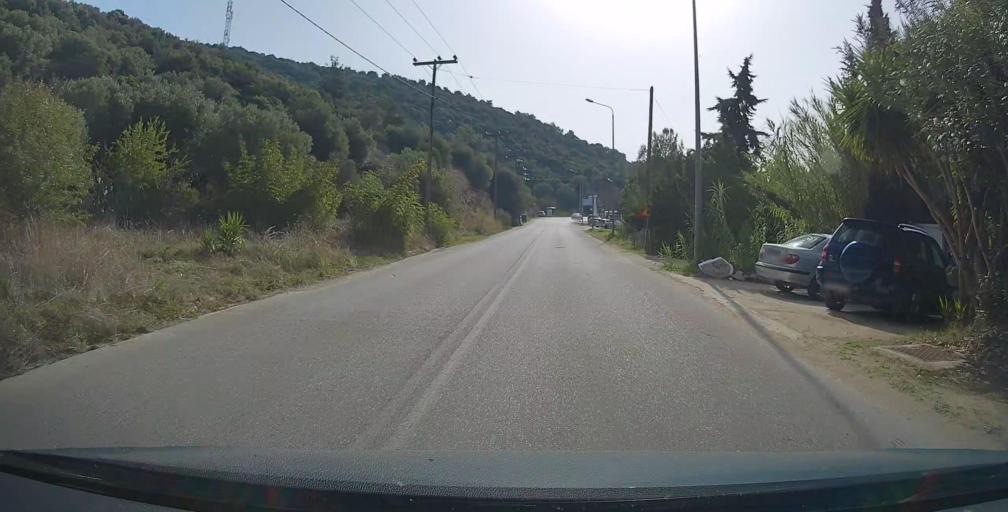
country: GR
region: Central Macedonia
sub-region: Nomos Chalkidikis
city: Sykia
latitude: 39.9723
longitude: 23.9172
